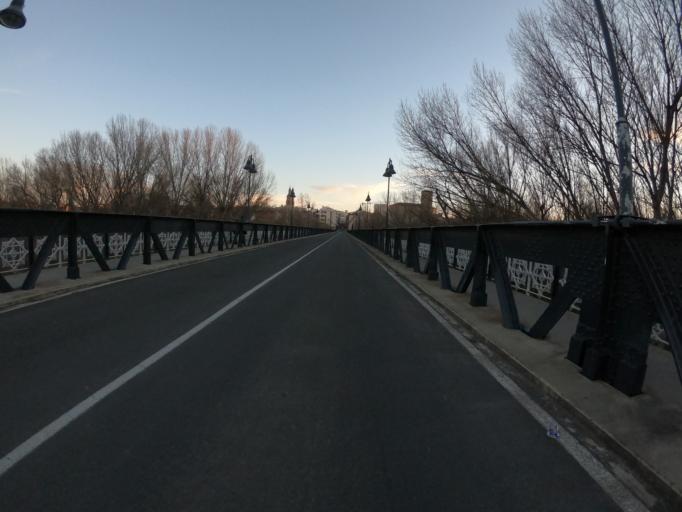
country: ES
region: La Rioja
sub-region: Provincia de La Rioja
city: Logrono
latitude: 42.4691
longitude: -2.4469
